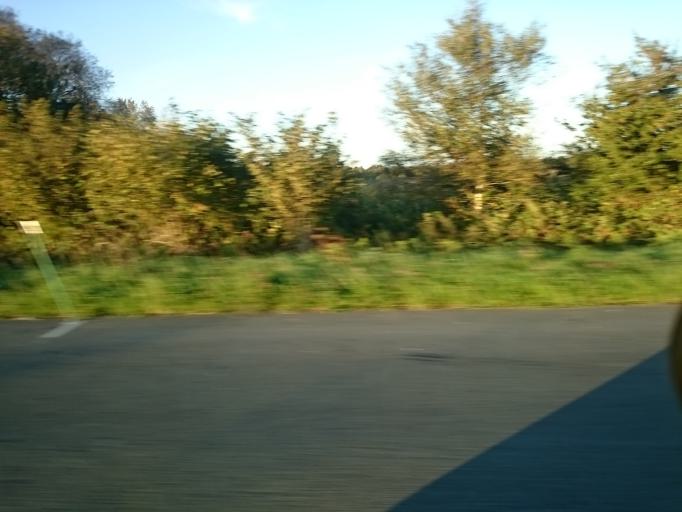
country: FR
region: Brittany
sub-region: Departement du Finistere
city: Plouigneau
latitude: 48.5797
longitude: -3.7408
